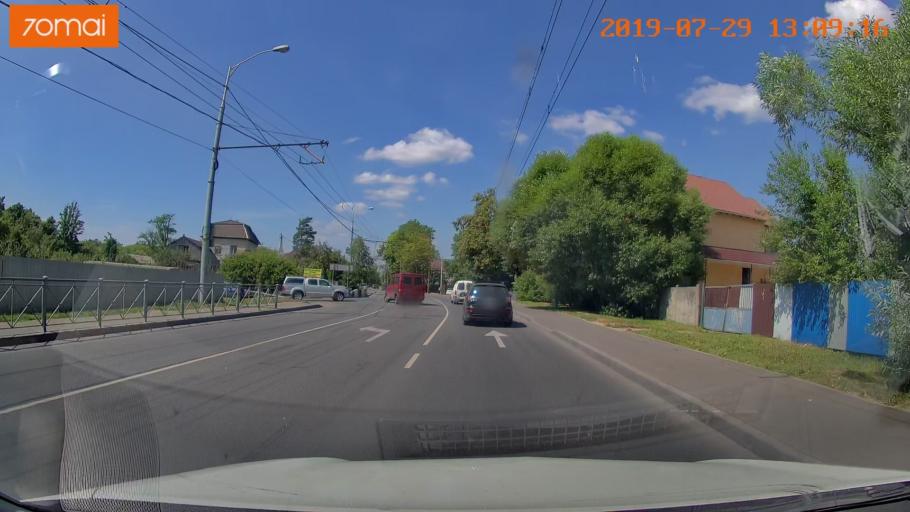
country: RU
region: Kaliningrad
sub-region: Gorod Kaliningrad
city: Kaliningrad
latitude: 54.7135
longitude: 20.4196
